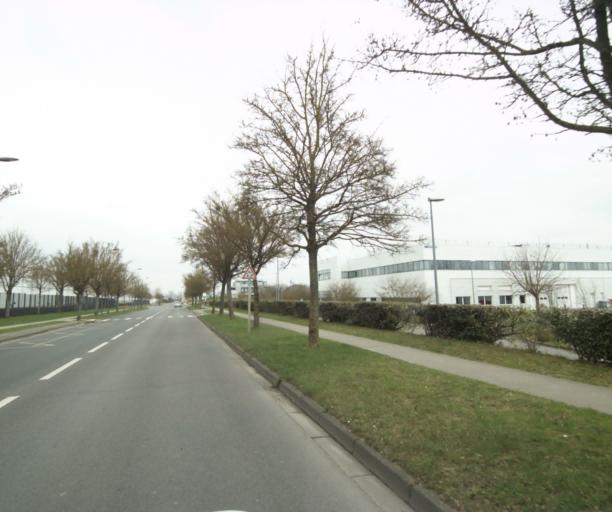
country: FR
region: Ile-de-France
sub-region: Departement du Val-d'Oise
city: Vaureal
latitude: 49.0544
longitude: 2.0325
